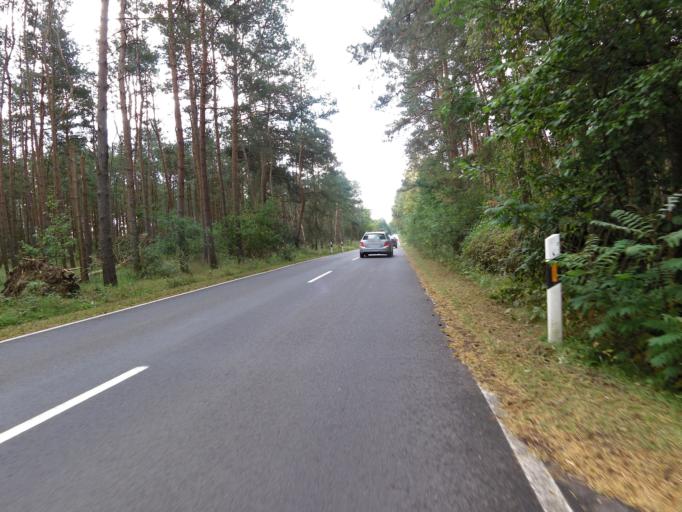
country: DE
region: Saxony-Anhalt
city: Gommern
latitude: 52.0609
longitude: 11.8611
